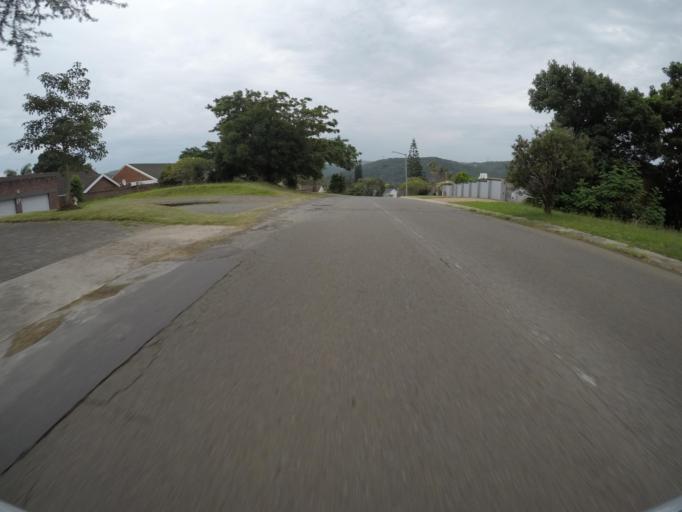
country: ZA
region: Eastern Cape
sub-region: Buffalo City Metropolitan Municipality
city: East London
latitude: -32.9480
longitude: 27.8982
